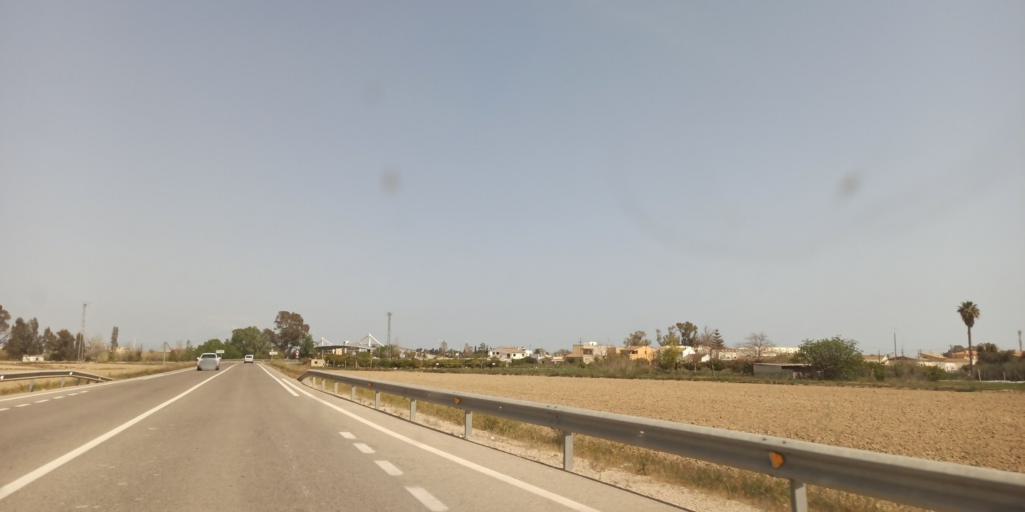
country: ES
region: Catalonia
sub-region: Provincia de Tarragona
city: Deltebre
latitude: 40.7087
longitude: 0.7135
